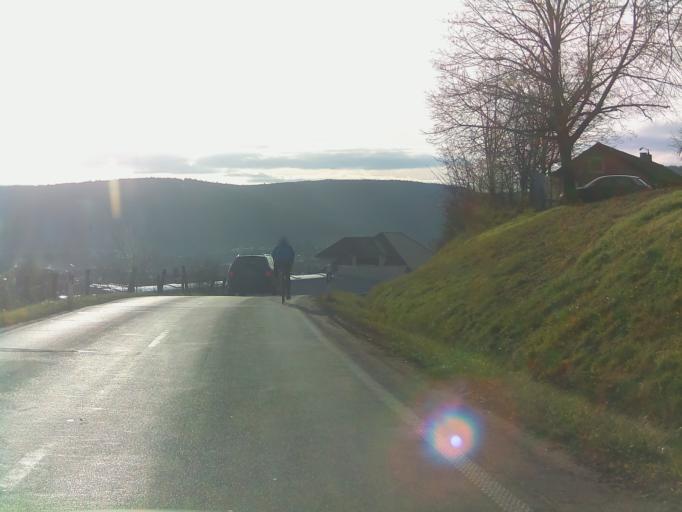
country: DE
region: Bavaria
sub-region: Regierungsbezirk Unterfranken
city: Grossheubach
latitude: 49.7340
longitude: 9.2319
